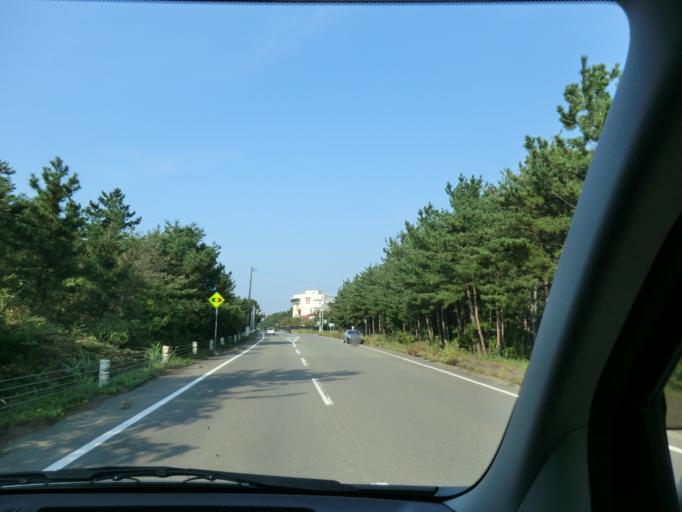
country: JP
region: Niigata
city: Kashiwazaki
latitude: 37.4250
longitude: 138.6078
